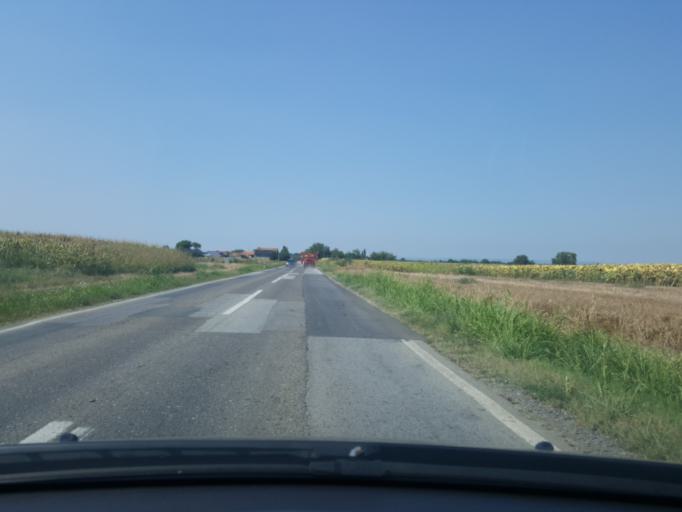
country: RS
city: Hrtkovci
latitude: 44.8637
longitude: 19.7716
